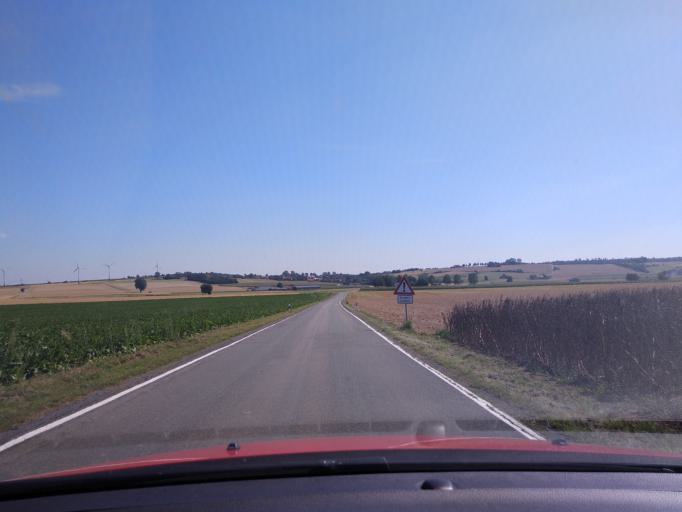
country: DE
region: North Rhine-Westphalia
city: Brakel
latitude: 51.6506
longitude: 9.1663
